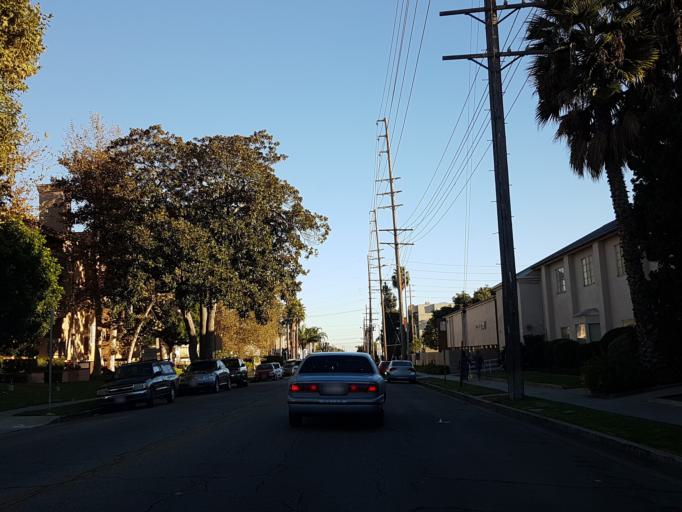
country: US
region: California
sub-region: Los Angeles County
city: Westwood, Los Angeles
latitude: 34.0425
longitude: -118.4550
